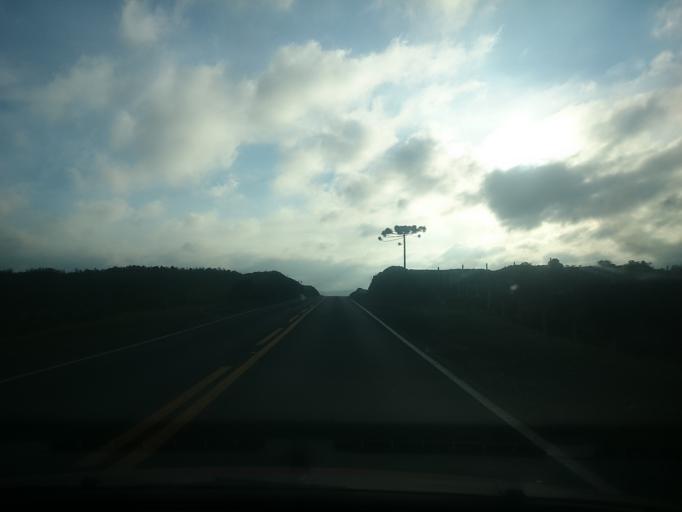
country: BR
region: Rio Grande do Sul
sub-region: Vacaria
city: Estrela
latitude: -28.1090
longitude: -50.6198
